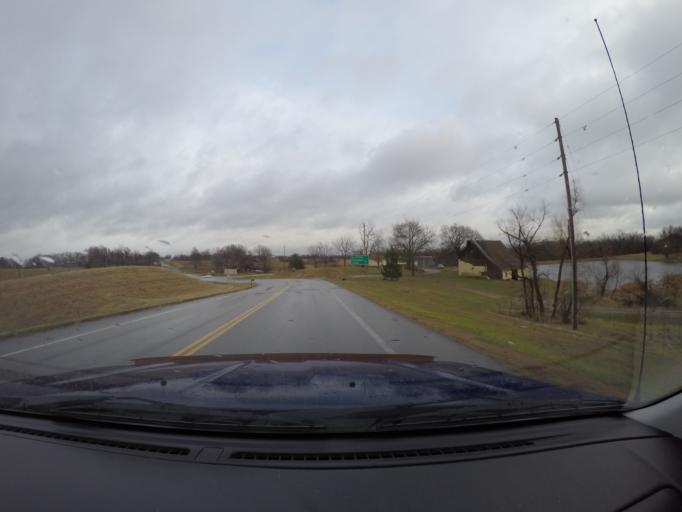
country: US
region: Kansas
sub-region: Leavenworth County
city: Leavenworth
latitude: 39.3681
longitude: -95.0516
